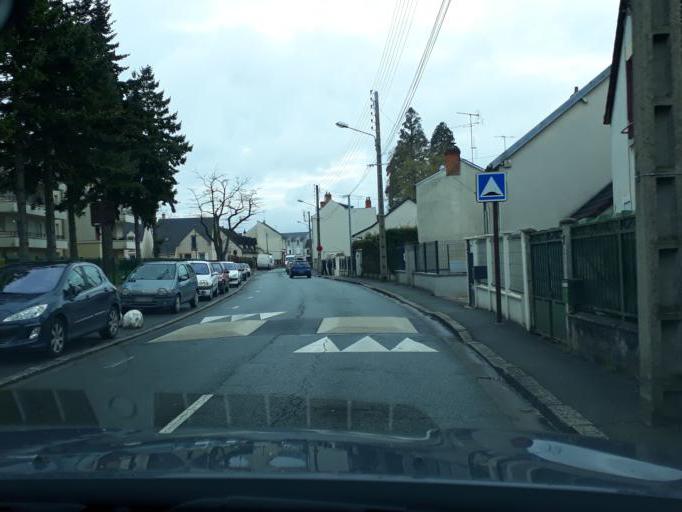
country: FR
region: Centre
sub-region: Departement du Loiret
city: Saint-Jean-de-la-Ruelle
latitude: 47.9120
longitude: 1.8816
